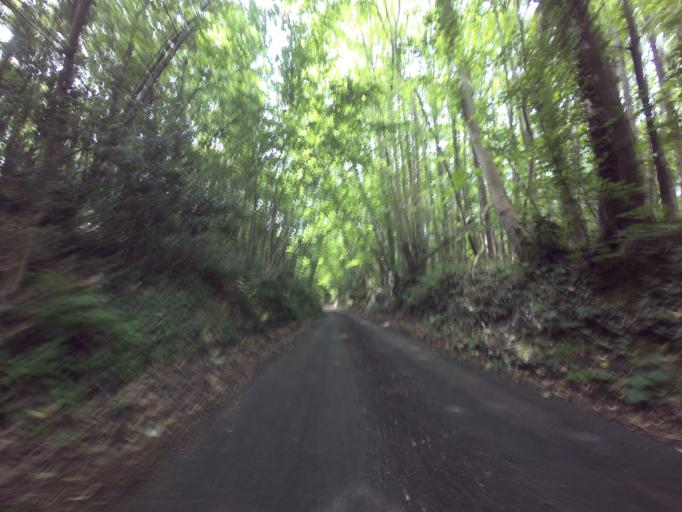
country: GB
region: England
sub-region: Kent
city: Halstead
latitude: 51.3494
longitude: 0.1414
